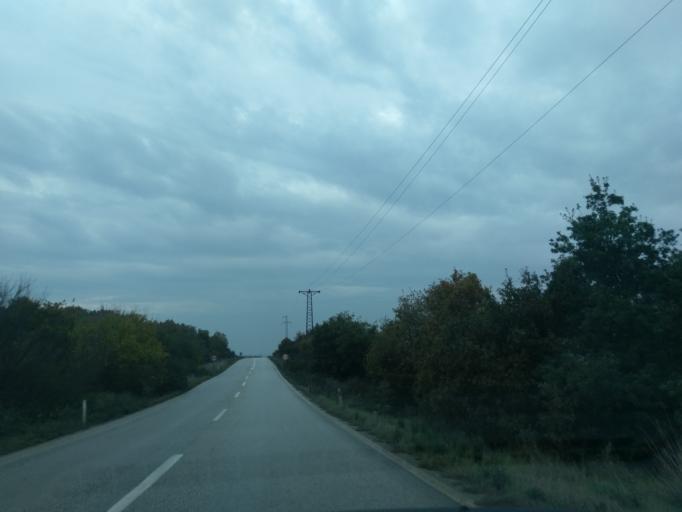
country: TR
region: Istanbul
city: Canta
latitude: 41.1562
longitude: 28.1068
